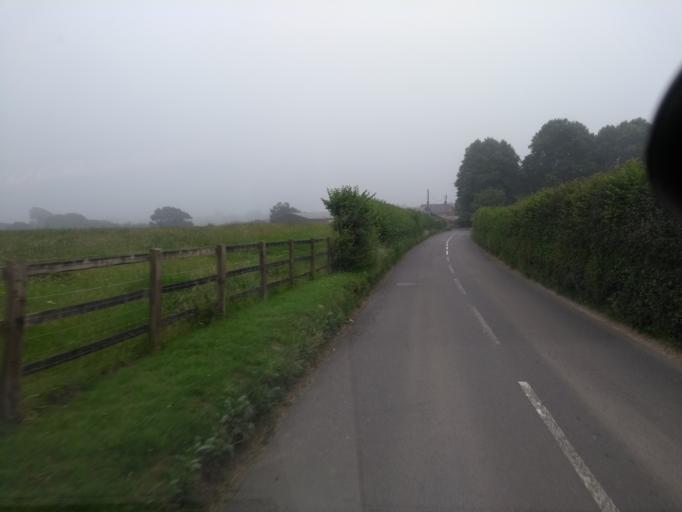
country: GB
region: England
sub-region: Dorset
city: Bridport
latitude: 50.7607
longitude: -2.7733
